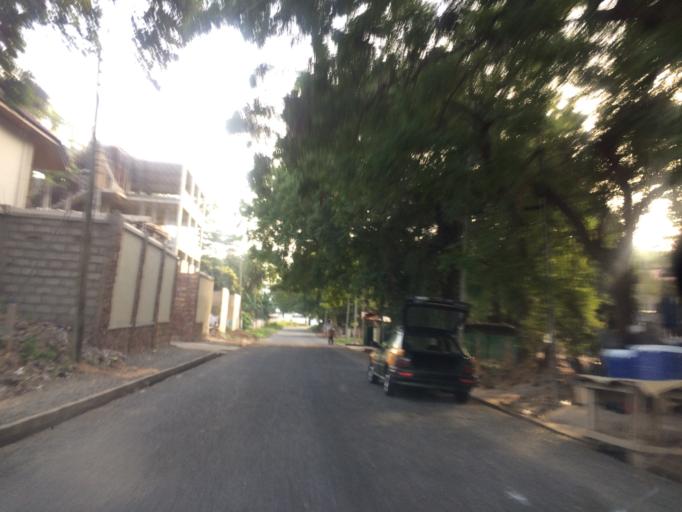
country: GH
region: Greater Accra
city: Accra
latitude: 5.5605
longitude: -0.2034
